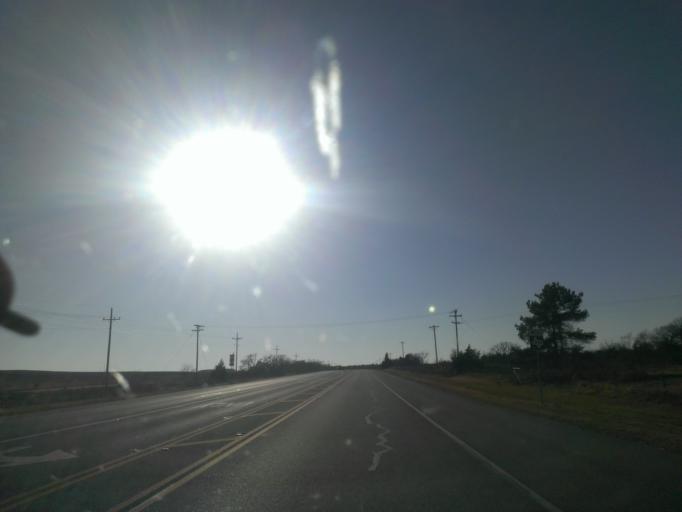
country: US
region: Texas
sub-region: Bastrop County
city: Elgin
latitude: 30.3800
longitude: -97.2446
